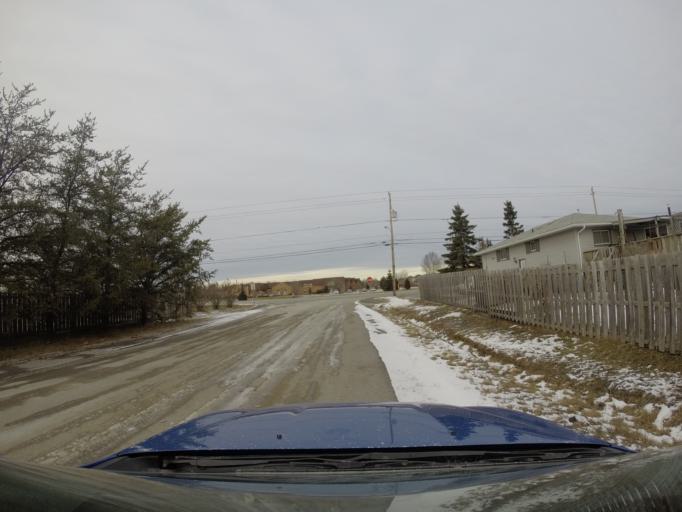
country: CA
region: Ontario
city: Greater Sudbury
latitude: 46.6103
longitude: -81.0264
